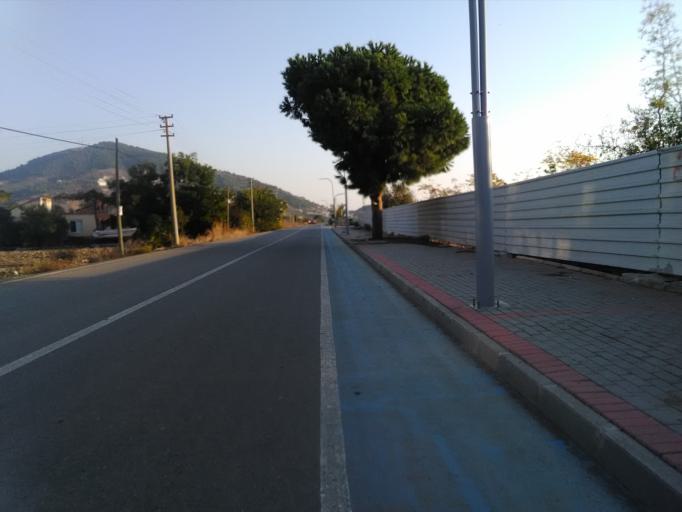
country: TR
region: Antalya
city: Gazipasa
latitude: 36.2517
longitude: 32.2924
